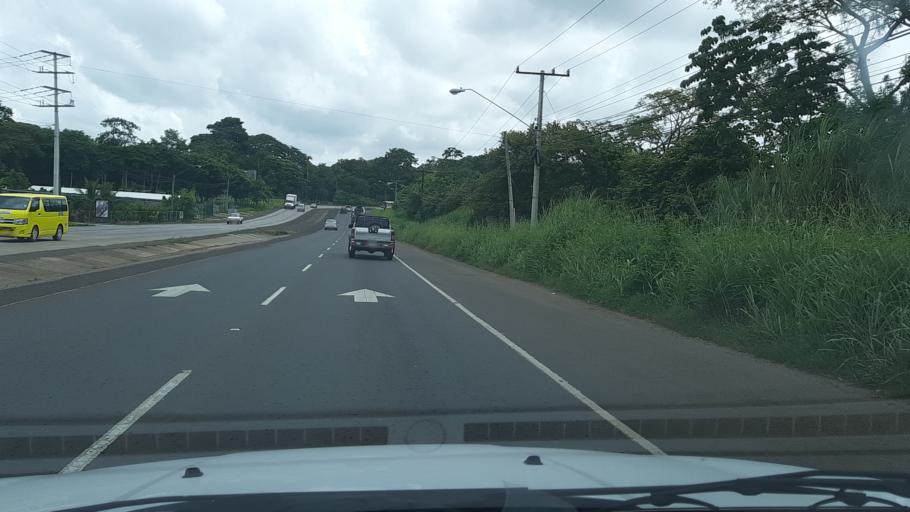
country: PA
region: Panama
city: La Chorrera
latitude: 8.8960
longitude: -79.7590
